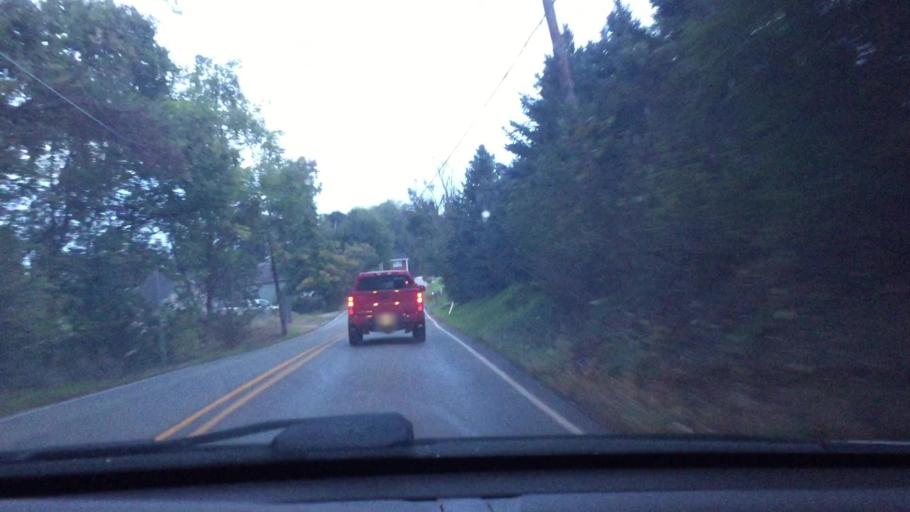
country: US
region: Pennsylvania
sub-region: Washington County
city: East Washington
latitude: 40.1836
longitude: -80.1818
